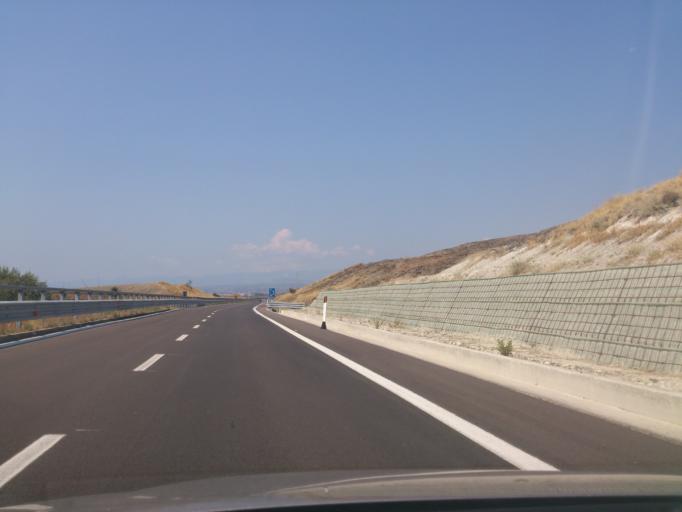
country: IT
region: Calabria
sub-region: Provincia di Reggio Calabria
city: Roccella Ionica
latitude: 38.3216
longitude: 16.3829
